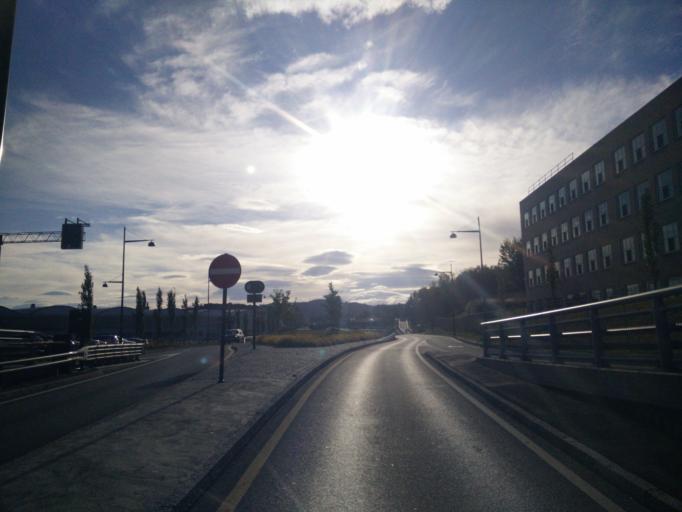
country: NO
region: Sor-Trondelag
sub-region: Trondheim
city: Trondheim
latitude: 63.4346
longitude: 10.4585
